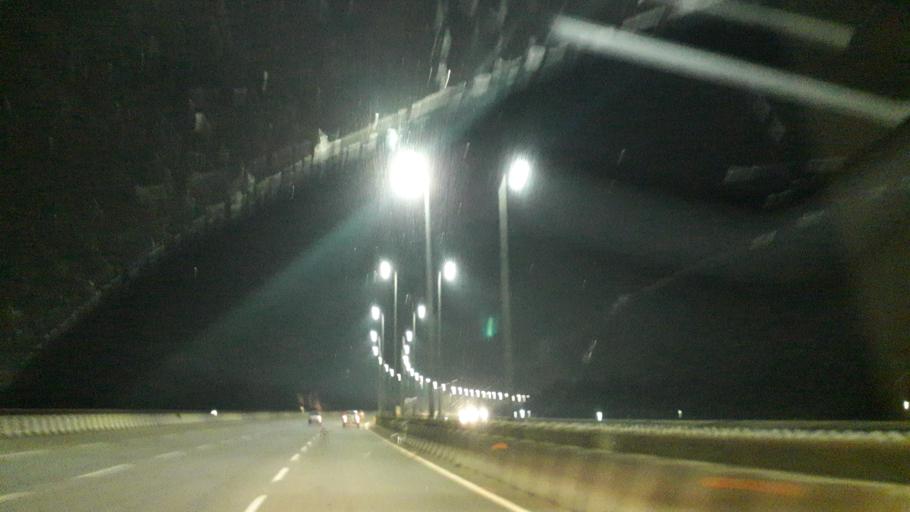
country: IN
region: Telangana
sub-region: Hyderabad
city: Hyderabad
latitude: 17.3254
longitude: 78.3746
